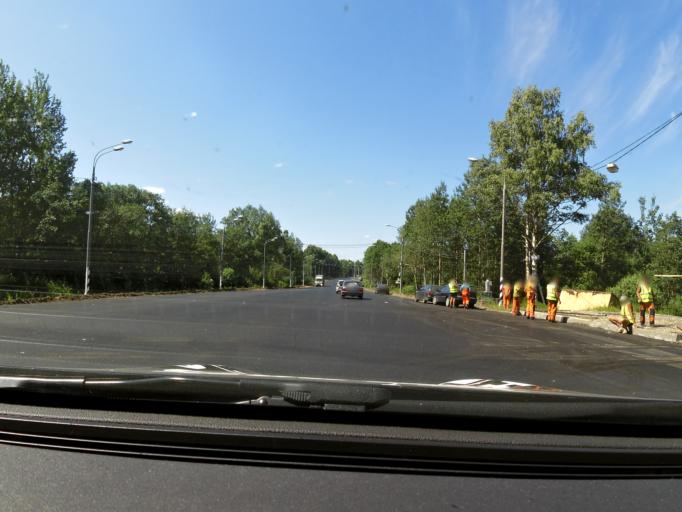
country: RU
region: Novgorod
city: Valday
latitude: 57.9538
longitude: 33.2671
